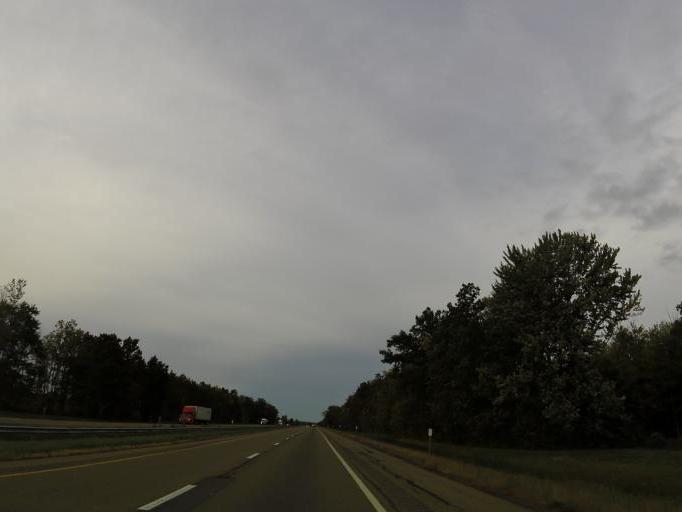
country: US
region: New York
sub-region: Chautauqua County
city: Silver Creek
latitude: 42.4937
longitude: -79.2424
